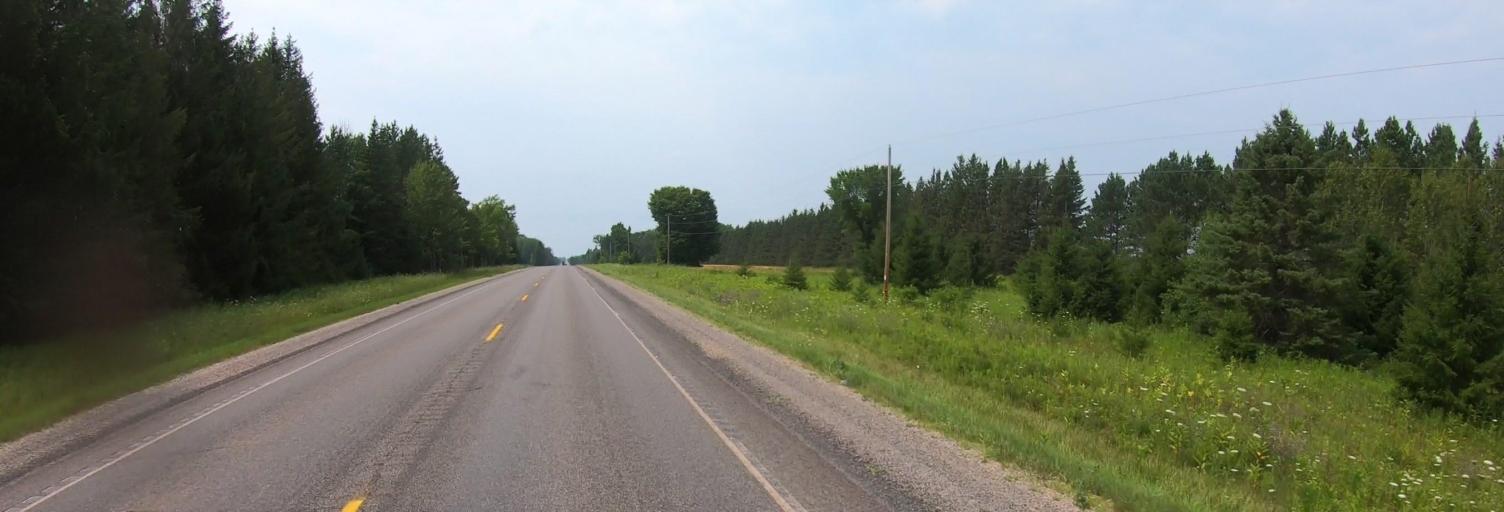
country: US
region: Michigan
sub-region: Alger County
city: Munising
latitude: 46.3330
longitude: -86.8915
